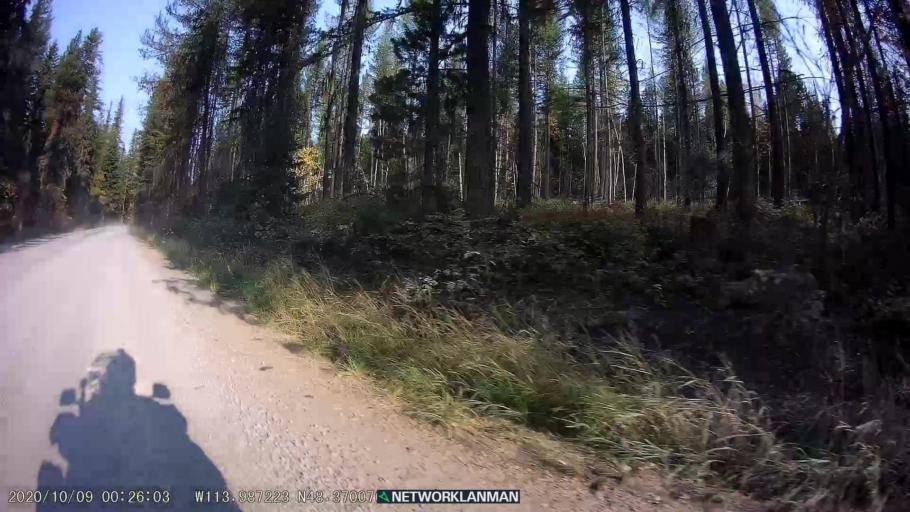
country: US
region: Montana
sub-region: Flathead County
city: Columbia Falls
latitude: 48.3709
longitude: -113.9887
